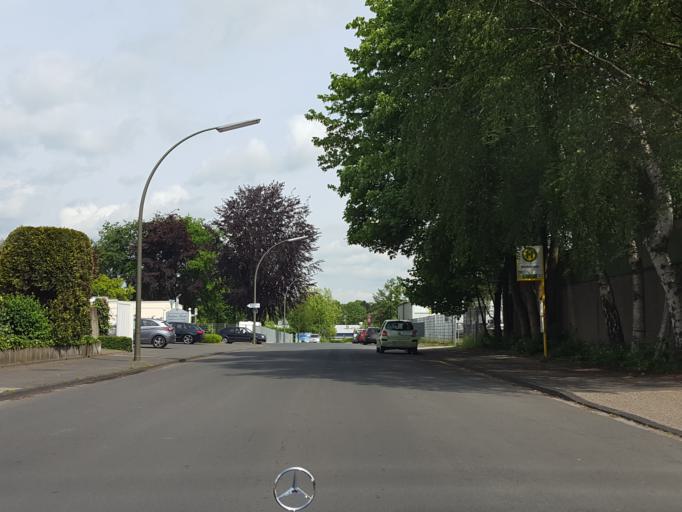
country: DE
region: North Rhine-Westphalia
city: Oer-Erkenschwick
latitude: 51.6343
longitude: 7.2741
